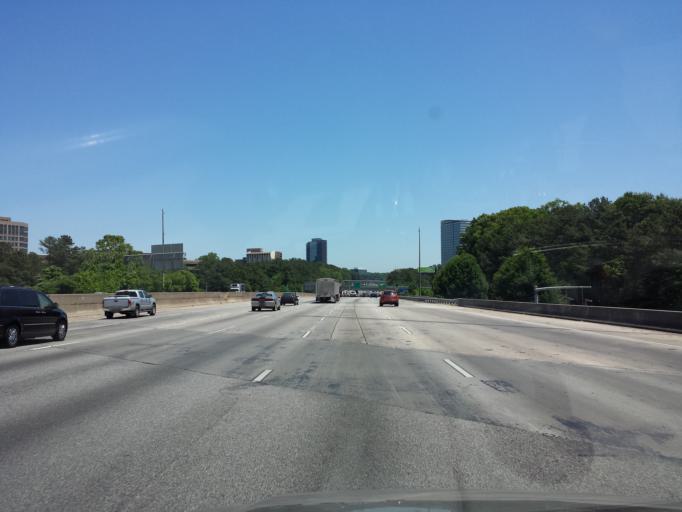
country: US
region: Georgia
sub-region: Fulton County
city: Sandy Springs
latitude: 33.9134
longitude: -84.3529
